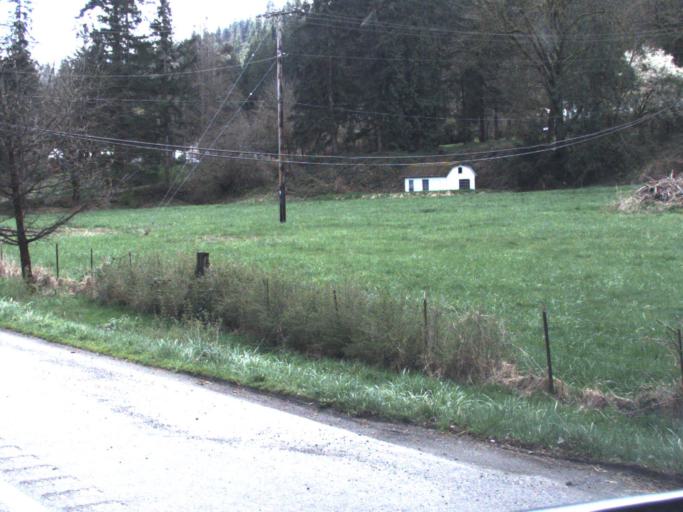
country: US
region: Washington
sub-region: King County
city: Maple Valley
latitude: 47.4312
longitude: -122.0573
